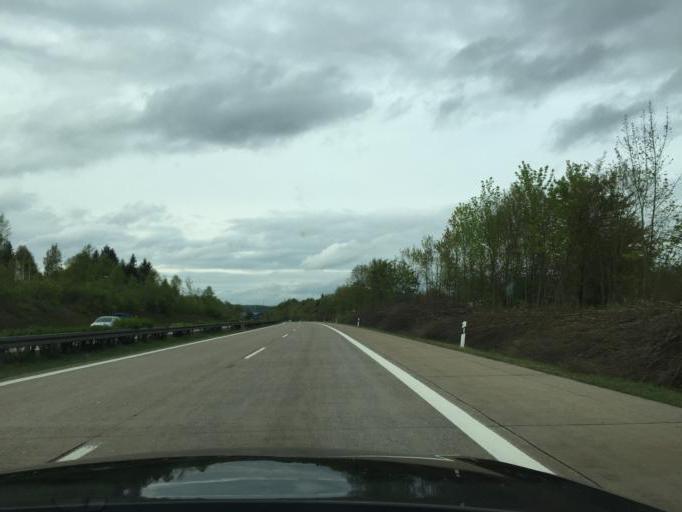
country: DE
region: Baden-Wuerttemberg
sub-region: Regierungsbezirk Stuttgart
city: Ellenberg
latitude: 48.9833
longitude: 10.1948
